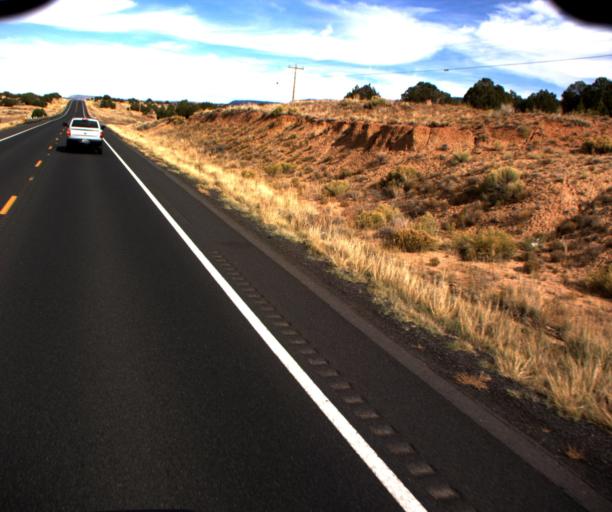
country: US
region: Arizona
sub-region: Navajo County
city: Kayenta
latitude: 36.4935
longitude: -110.6282
